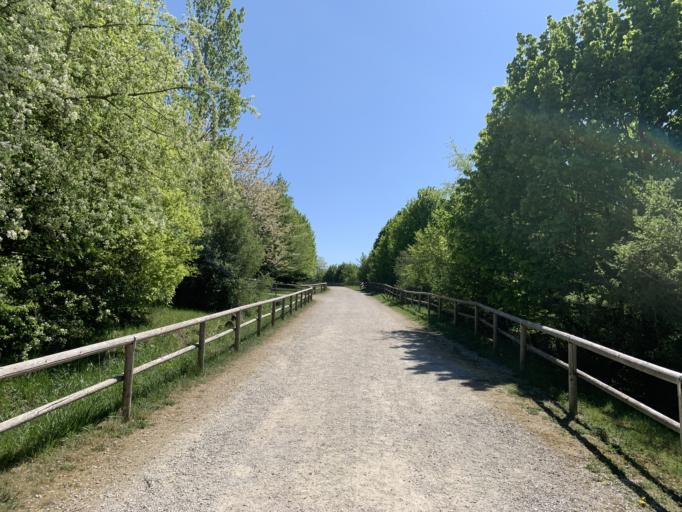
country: DE
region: Bavaria
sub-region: Swabia
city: Gersthofen
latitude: 48.4181
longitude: 10.8926
